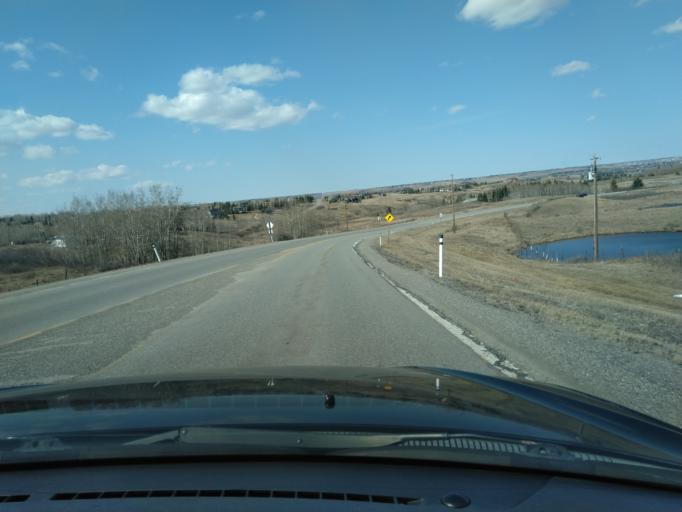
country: CA
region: Alberta
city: Cochrane
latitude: 51.0913
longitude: -114.3040
